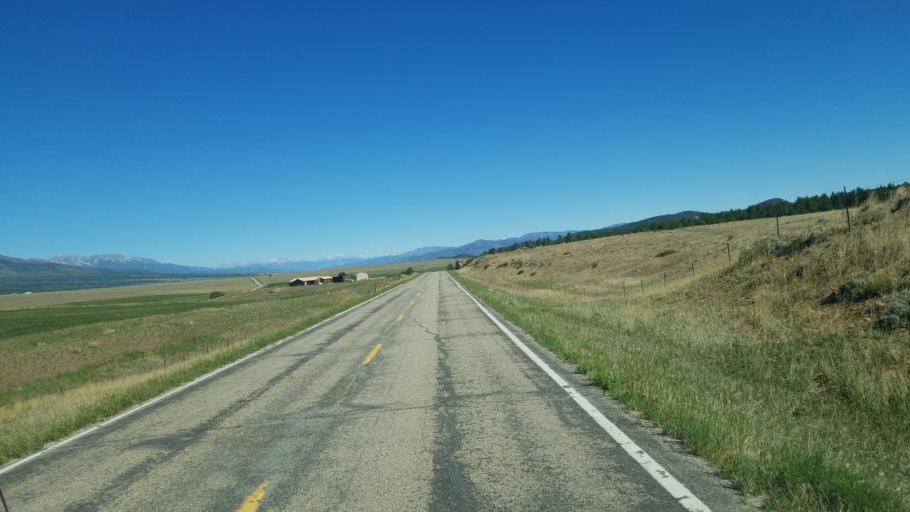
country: US
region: Colorado
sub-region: Custer County
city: Westcliffe
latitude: 38.2104
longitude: -105.5446
